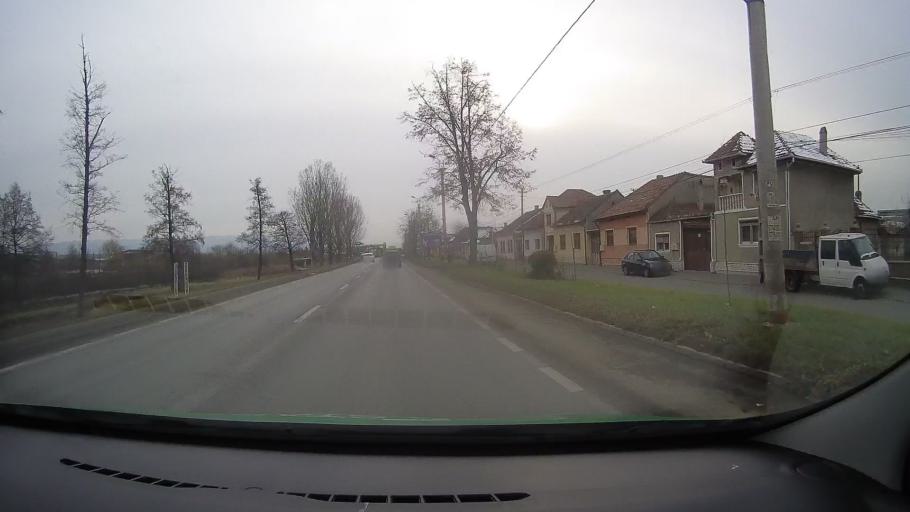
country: RO
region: Hunedoara
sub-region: Municipiul Orastie
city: Orastie
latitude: 45.8518
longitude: 23.2075
